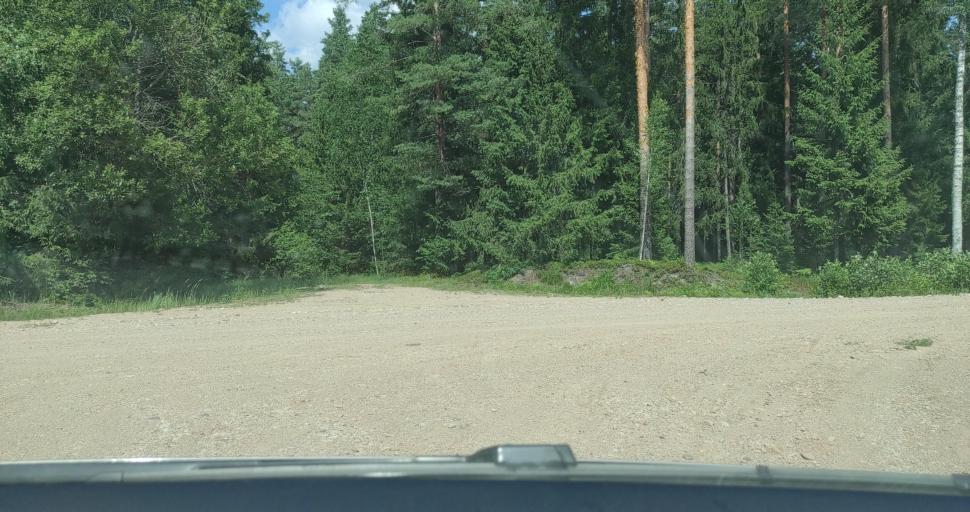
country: LV
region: Kuldigas Rajons
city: Kuldiga
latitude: 57.0674
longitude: 22.1935
